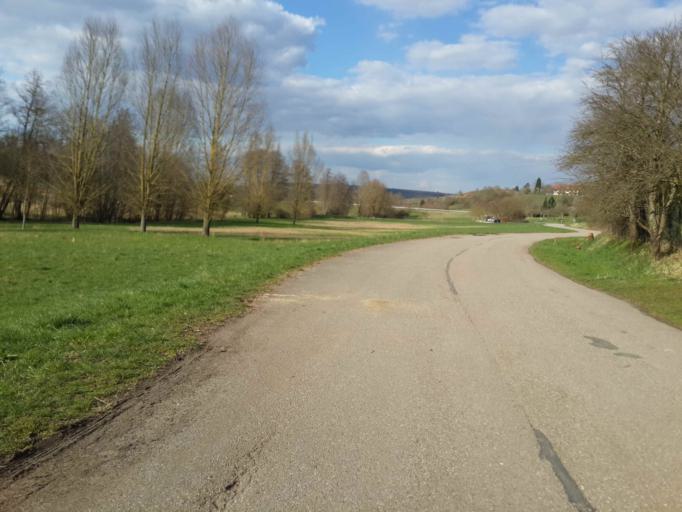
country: DE
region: Baden-Wuerttemberg
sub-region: Regierungsbezirk Stuttgart
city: Weinsberg
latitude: 49.1351
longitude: 9.2954
